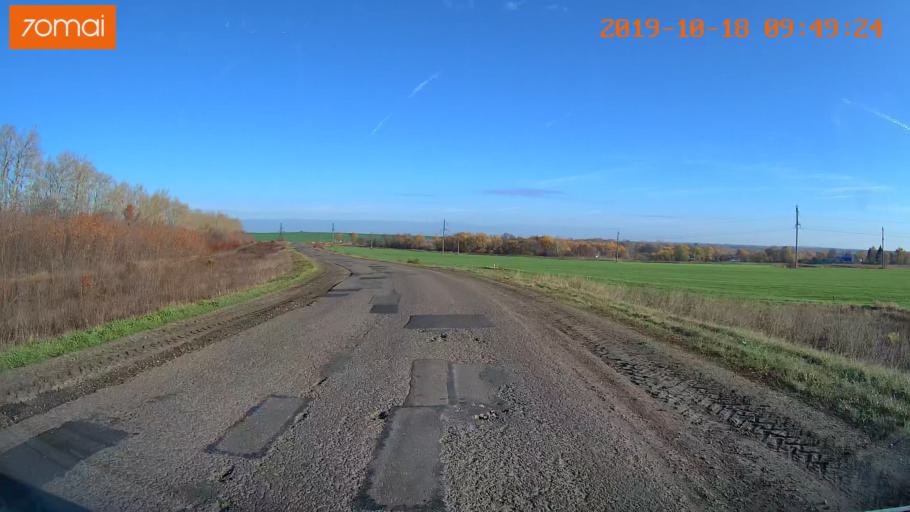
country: RU
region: Tula
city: Kazachka
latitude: 53.3175
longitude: 38.2677
